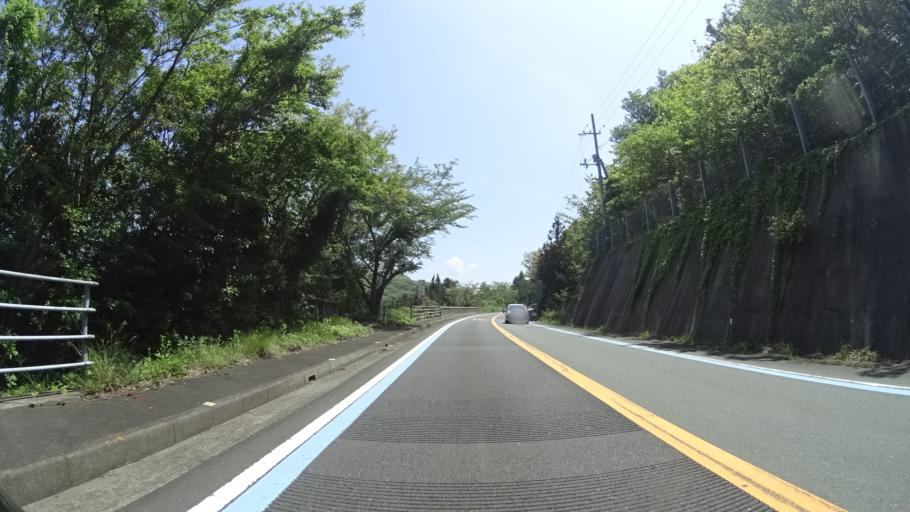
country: JP
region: Ehime
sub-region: Nishiuwa-gun
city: Ikata-cho
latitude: 33.4465
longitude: 132.2627
